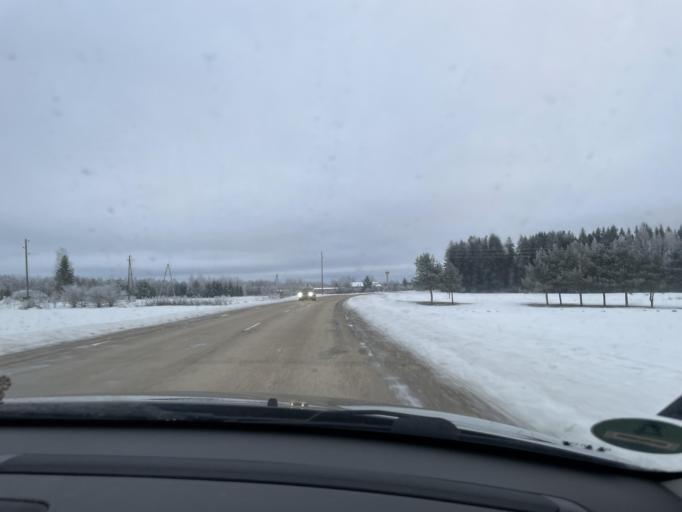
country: LV
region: Rezekne
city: Rezekne
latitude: 56.4958
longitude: 27.4196
